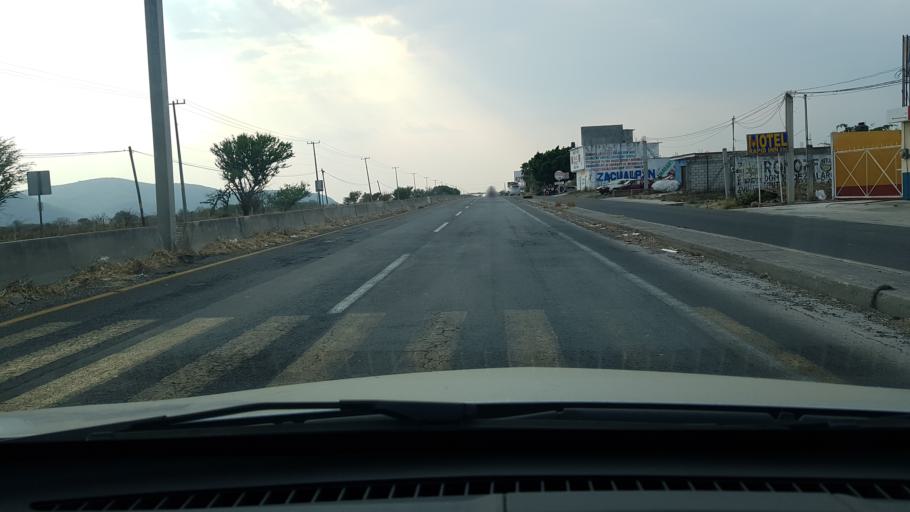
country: MX
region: Morelos
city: Amayuca
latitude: 18.7349
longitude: -98.8195
